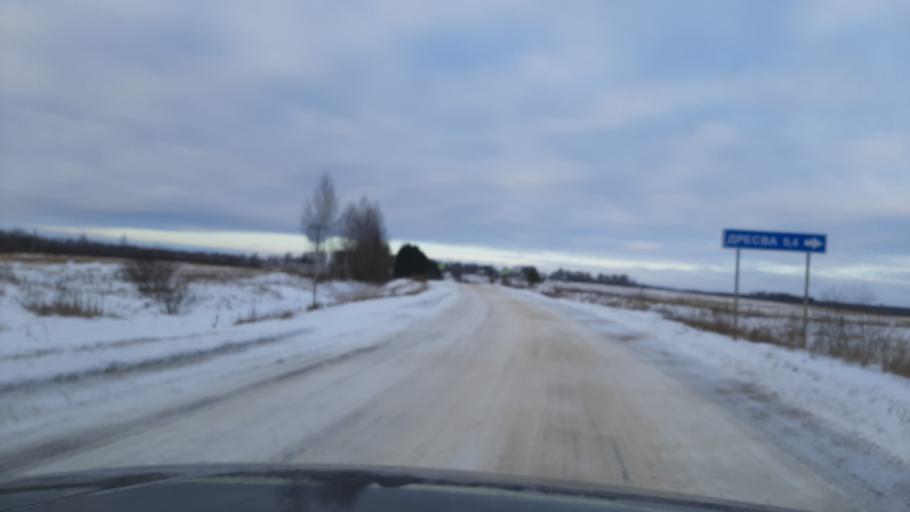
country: RU
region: Kostroma
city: Kosmynino
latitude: 57.4822
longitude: 40.7912
